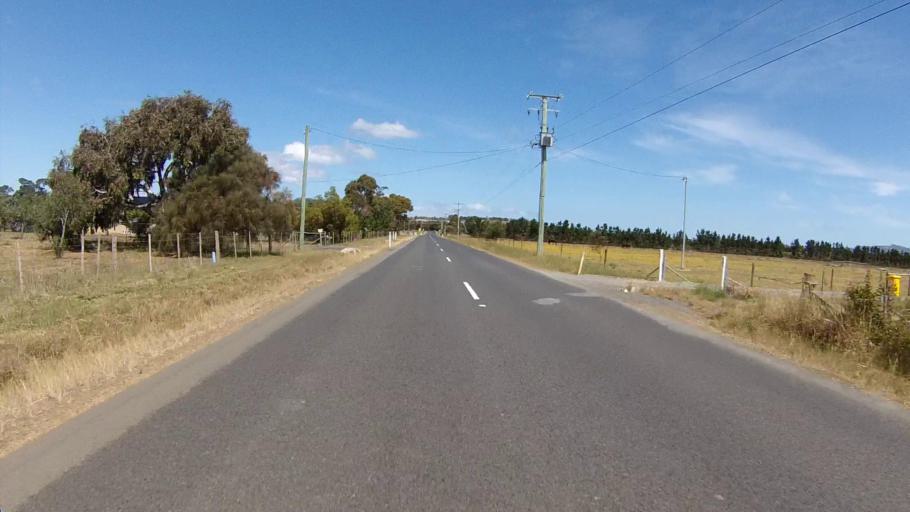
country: AU
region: Tasmania
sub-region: Sorell
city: Sorell
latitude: -42.7752
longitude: 147.5198
